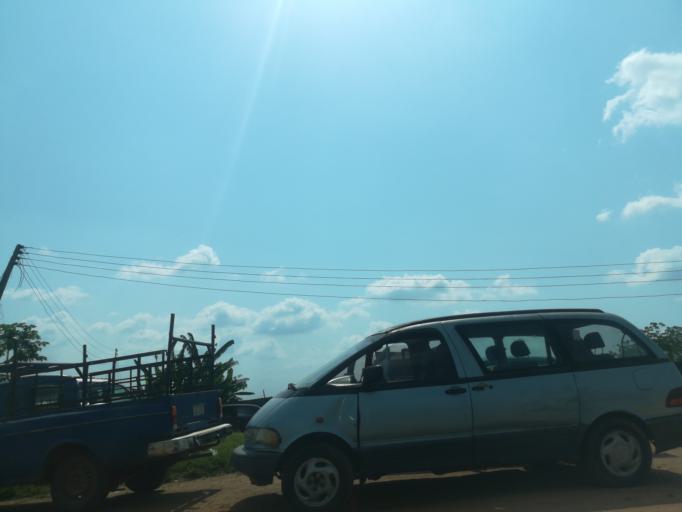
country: NG
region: Oyo
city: Moniya
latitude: 7.5196
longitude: 3.9127
